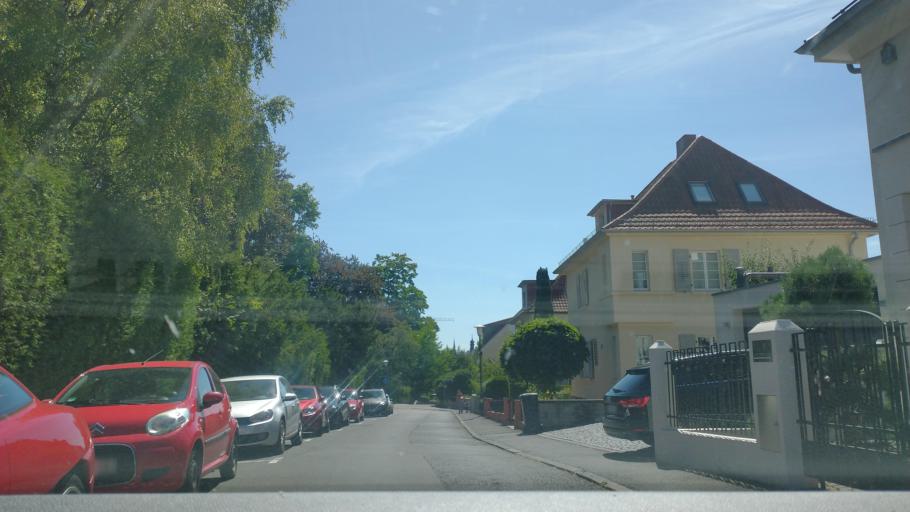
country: DE
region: Hesse
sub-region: Regierungsbezirk Kassel
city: Fulda
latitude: 50.5581
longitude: 9.6716
